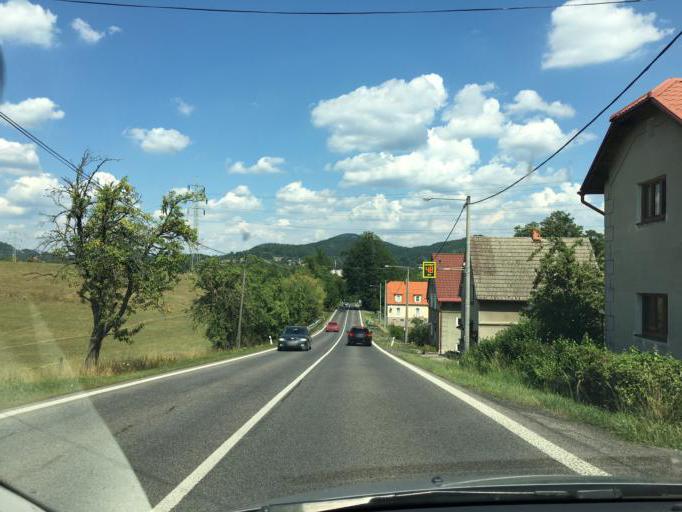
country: CZ
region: Ustecky
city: Ceska Kamenice
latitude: 50.7936
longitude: 14.3979
